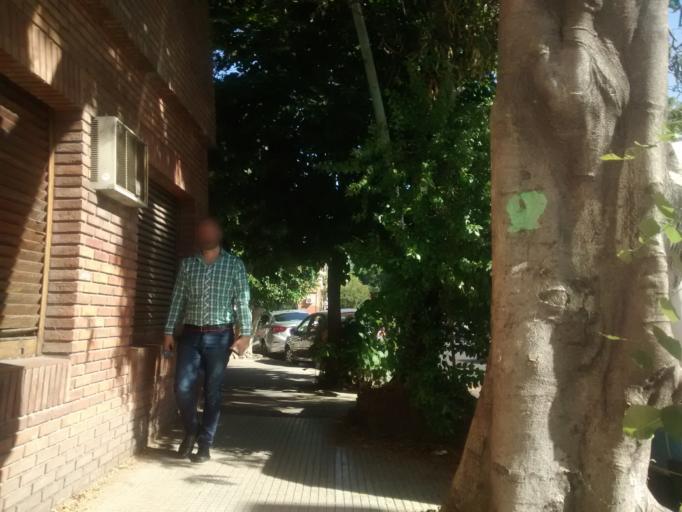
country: AR
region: Buenos Aires F.D.
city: Villa Santa Rita
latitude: -34.6085
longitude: -58.4465
